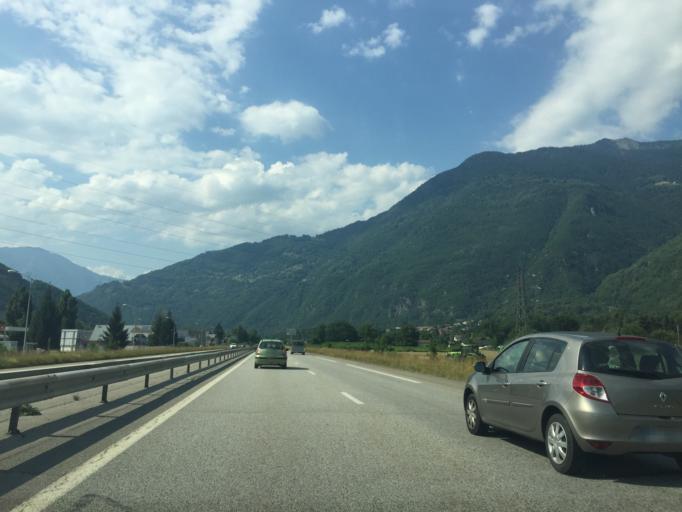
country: FR
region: Rhone-Alpes
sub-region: Departement de la Savoie
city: La Bathie
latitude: 45.6398
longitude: 6.4405
